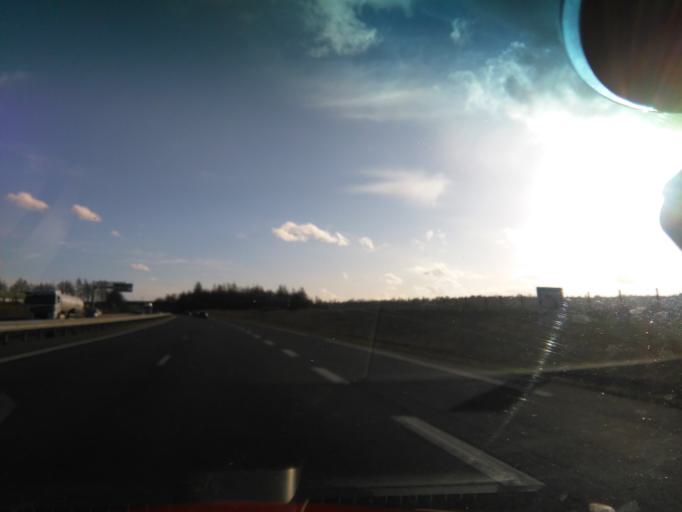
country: FR
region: Lower Normandy
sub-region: Departement du Calvados
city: Falaise
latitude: 48.9106
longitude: -0.2110
